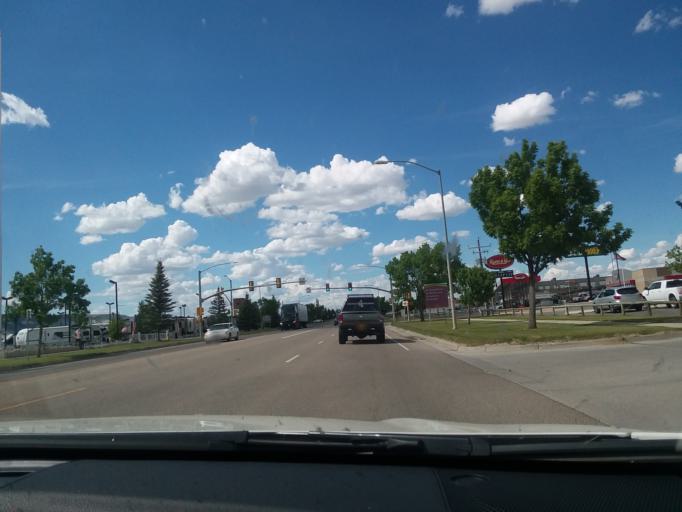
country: US
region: Wyoming
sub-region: Sweetwater County
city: Rock Springs
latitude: 41.6165
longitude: -109.2317
